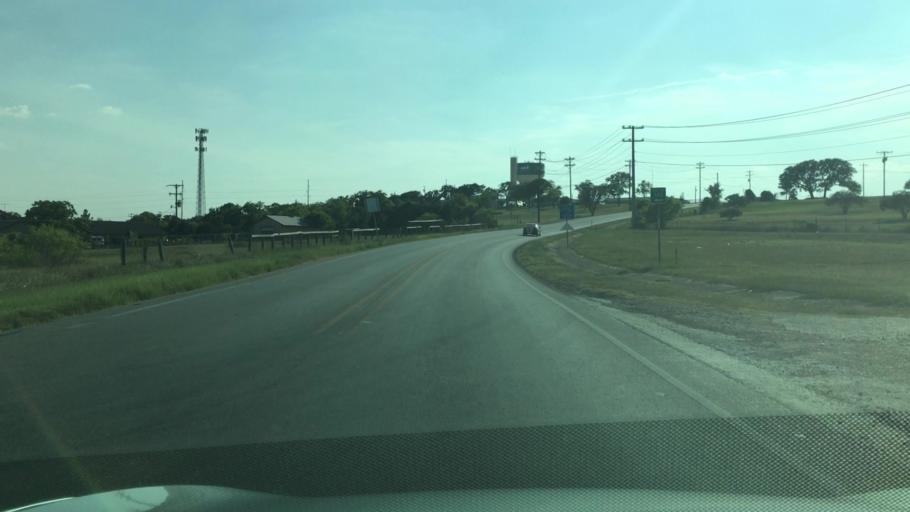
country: US
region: Texas
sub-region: Hays County
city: Buda
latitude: 30.0959
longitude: -97.8874
